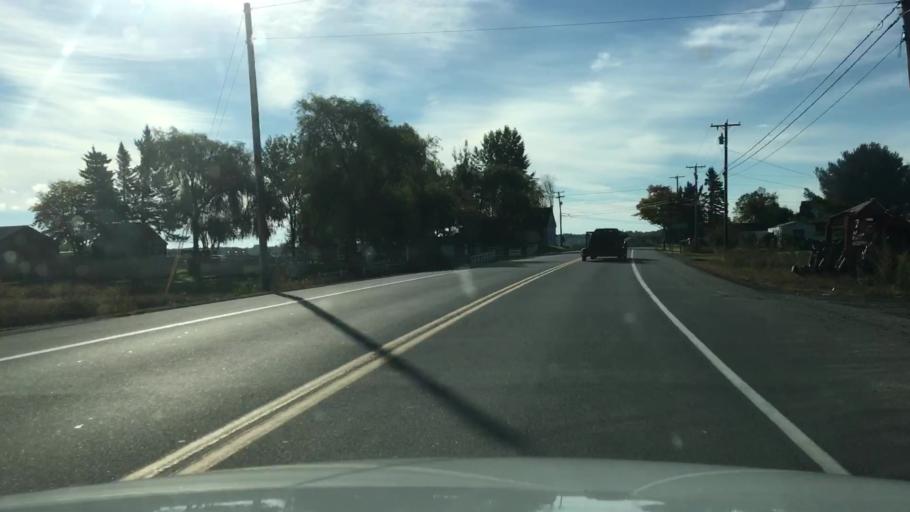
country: US
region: Maine
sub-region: Knox County
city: Warren
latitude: 44.0825
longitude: -69.2264
